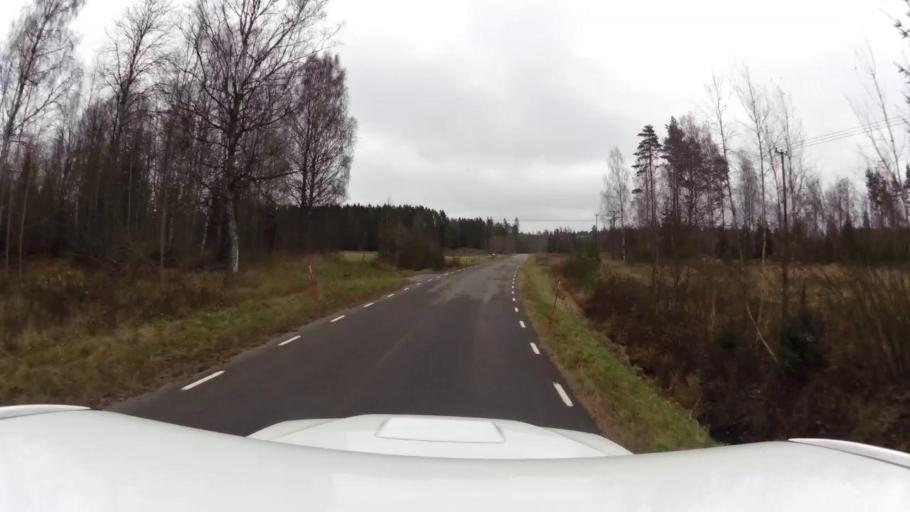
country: SE
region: OEstergoetland
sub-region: Kinda Kommun
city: Rimforsa
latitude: 58.1472
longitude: 15.4770
